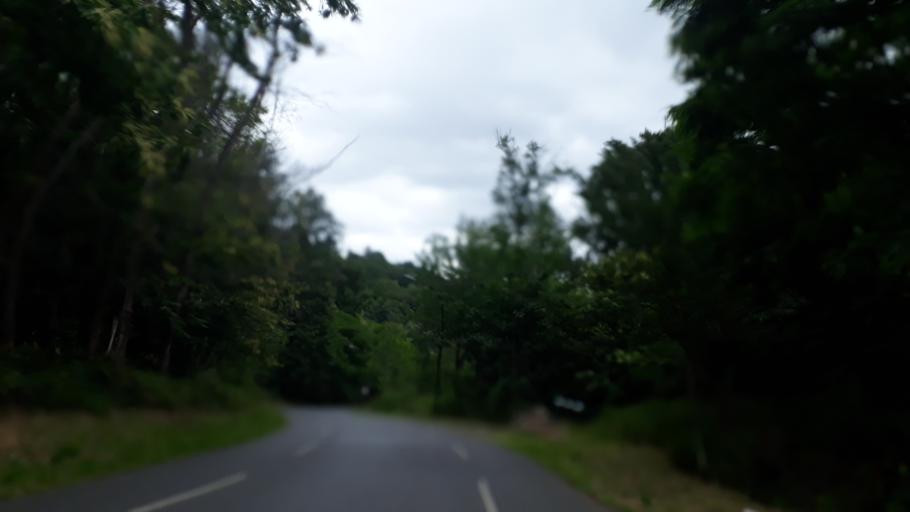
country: FR
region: Ile-de-France
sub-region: Departement de l'Essonne
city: La Ville-du-Bois
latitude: 48.6695
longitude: 2.2625
